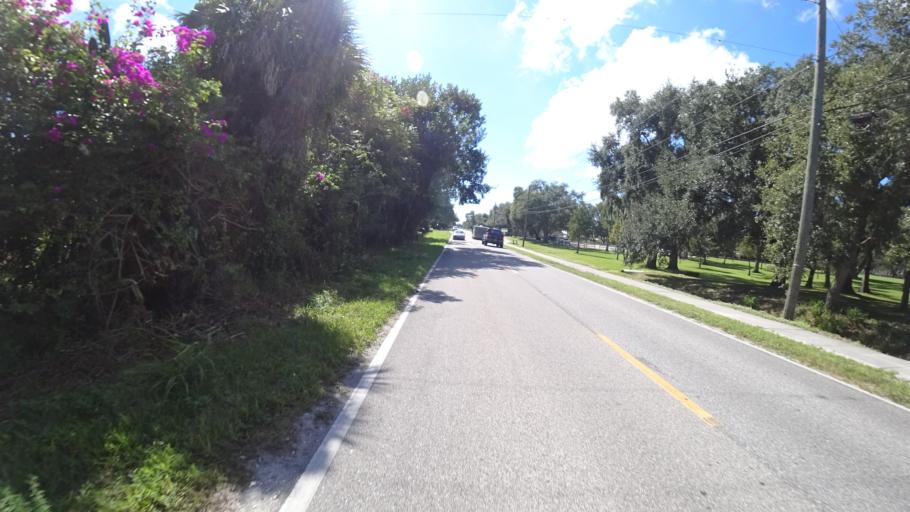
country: US
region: Florida
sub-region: Manatee County
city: West Bradenton
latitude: 27.4731
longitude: -82.6123
